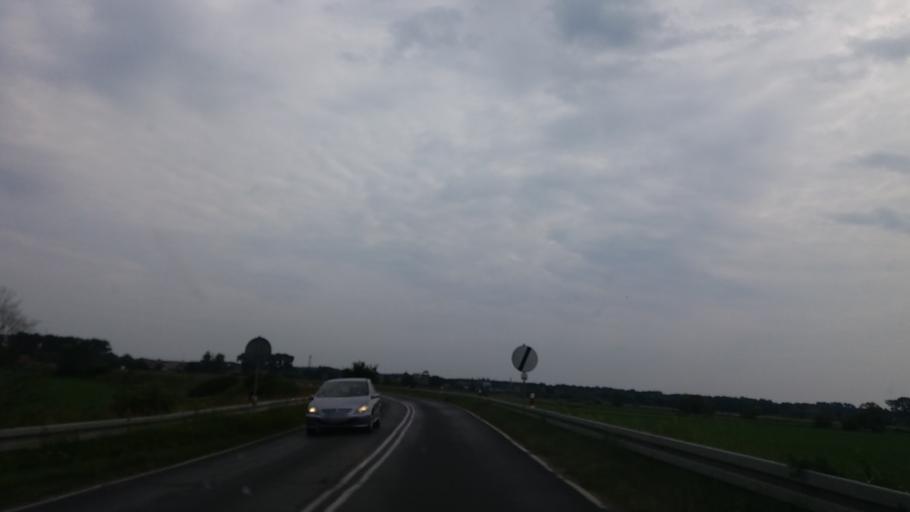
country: PL
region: Lubusz
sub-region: Powiat miedzyrzecki
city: Skwierzyna
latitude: 52.6056
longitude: 15.4856
